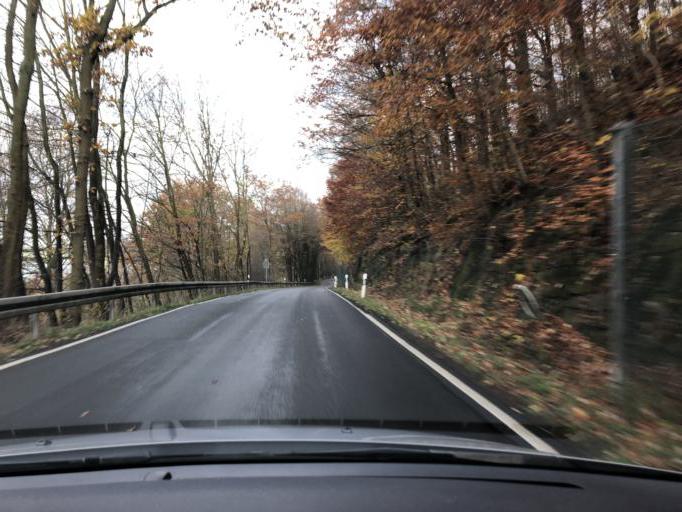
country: DE
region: Saxony
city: Nerchau
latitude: 51.2556
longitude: 12.7822
